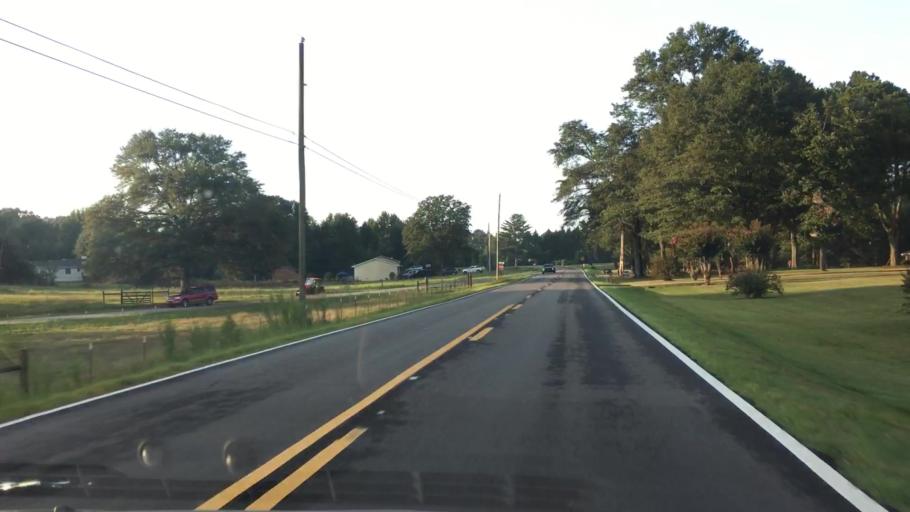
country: US
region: Georgia
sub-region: Henry County
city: McDonough
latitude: 33.4735
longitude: -84.1943
